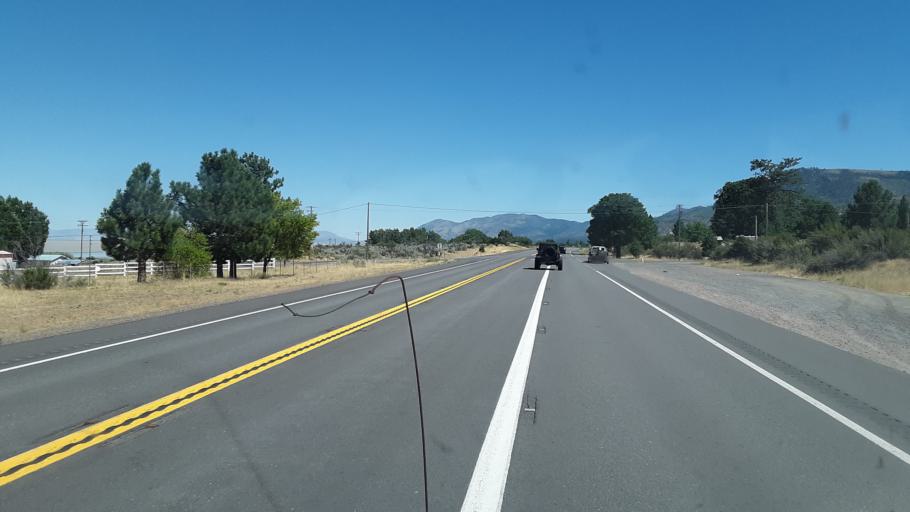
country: US
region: California
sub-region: Lassen County
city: Janesville
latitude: 40.2663
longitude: -120.4746
